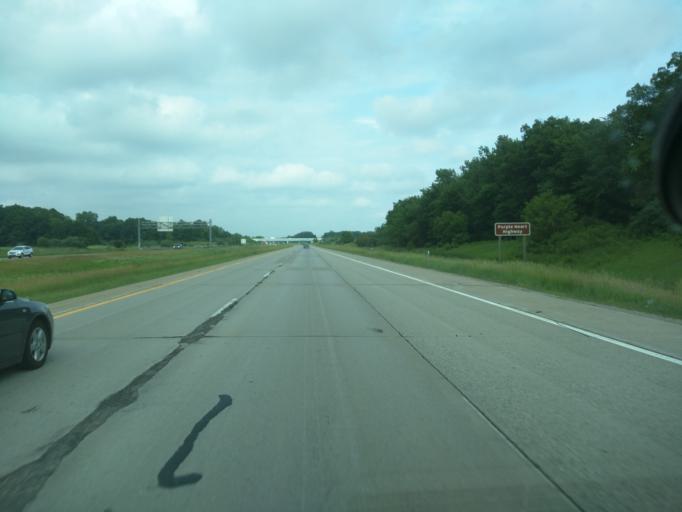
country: US
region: Michigan
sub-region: Clinton County
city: Bath
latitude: 42.8022
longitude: -84.4929
